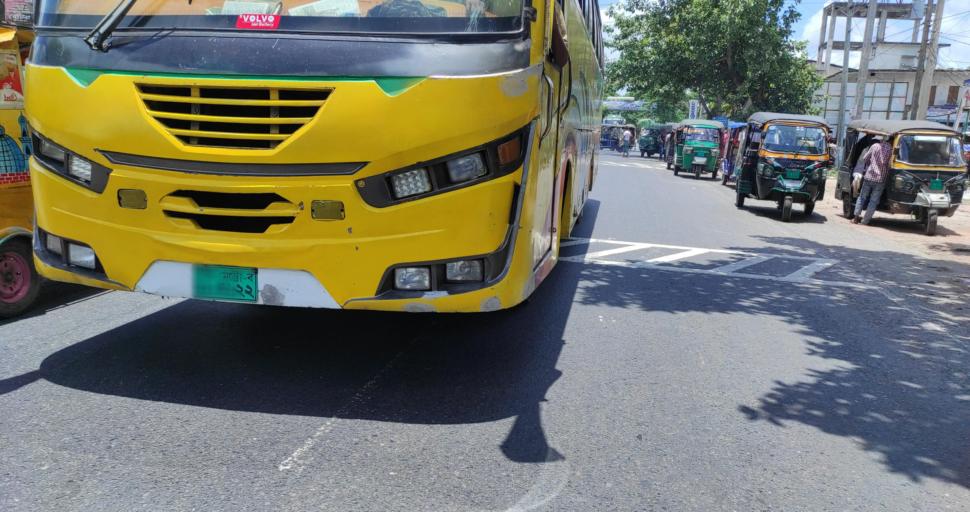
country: BD
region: Barisal
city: Gaurnadi
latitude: 22.8318
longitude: 90.2562
